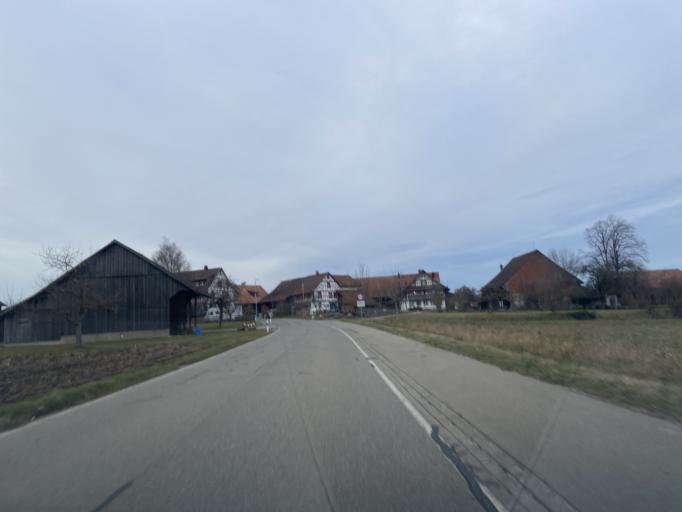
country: CH
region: Zurich
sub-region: Bezirk Winterthur
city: Brutten
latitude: 47.4772
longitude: 8.6654
